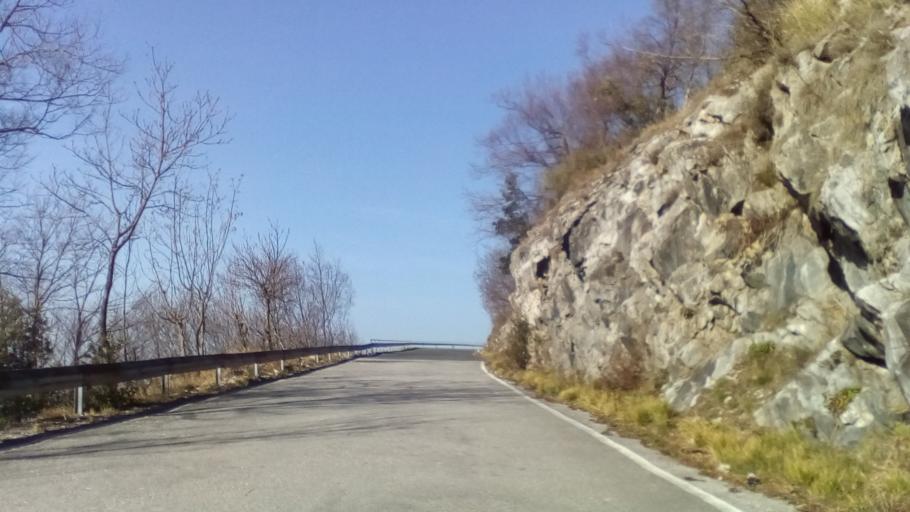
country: IT
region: Tuscany
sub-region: Provincia di Massa-Carrara
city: Montignoso
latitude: 44.0560
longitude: 10.1997
